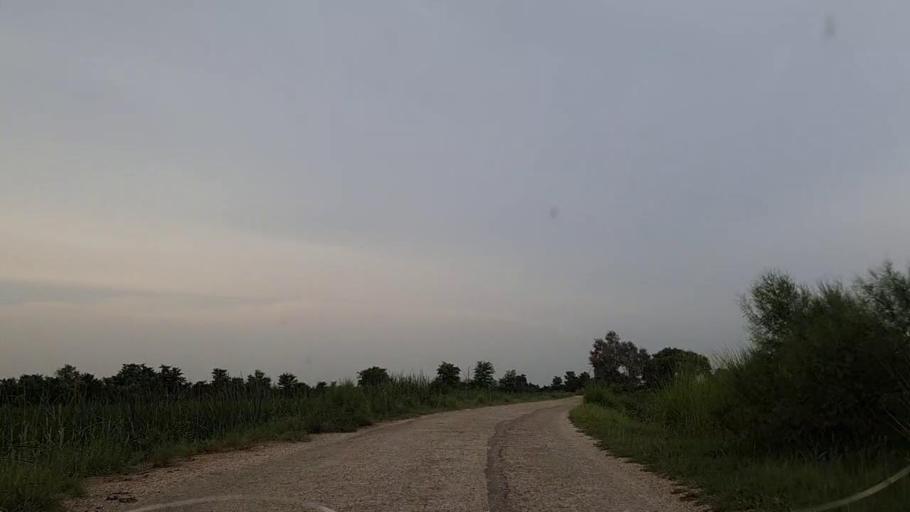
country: PK
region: Sindh
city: Mirpur Mathelo
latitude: 27.8745
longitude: 69.6358
